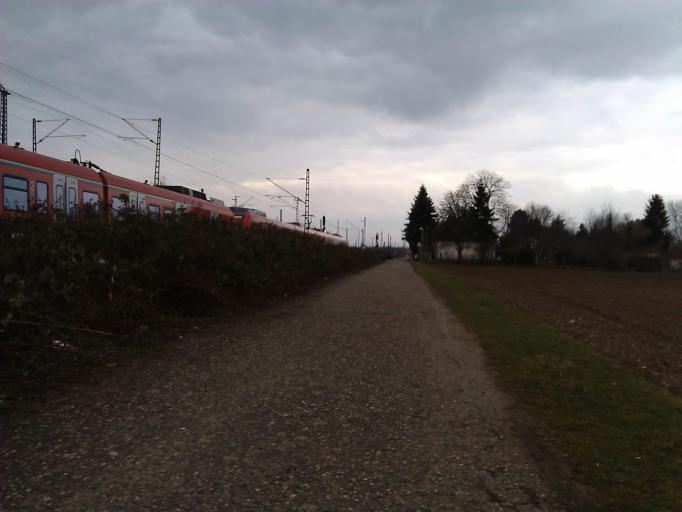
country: DE
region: Hesse
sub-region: Regierungsbezirk Darmstadt
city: Bischofsheim
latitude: 49.9872
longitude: 8.3711
